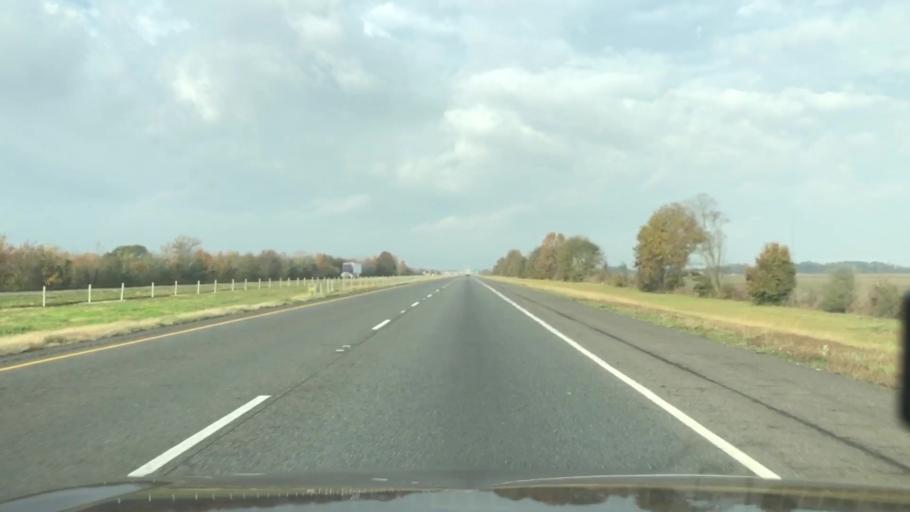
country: US
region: Louisiana
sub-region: Richland Parish
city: Delhi
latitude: 32.4279
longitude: -91.3945
